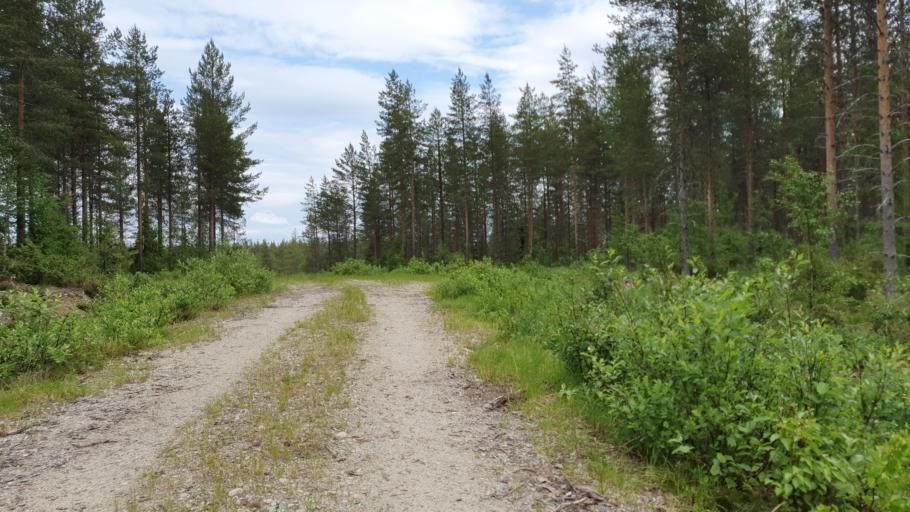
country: FI
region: Kainuu
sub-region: Kehys-Kainuu
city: Kuhmo
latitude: 64.4470
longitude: 29.7055
